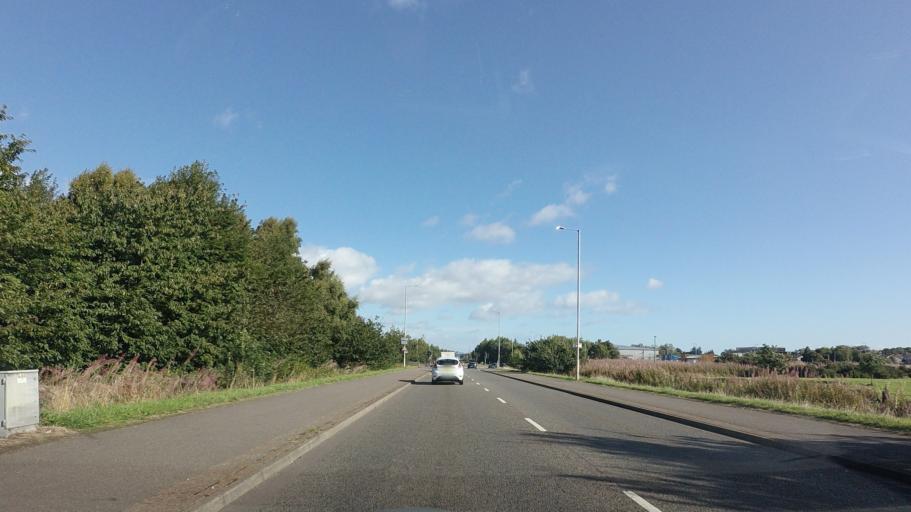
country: GB
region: Scotland
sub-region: Highland
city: Inverness
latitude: 57.4652
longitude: -4.1953
